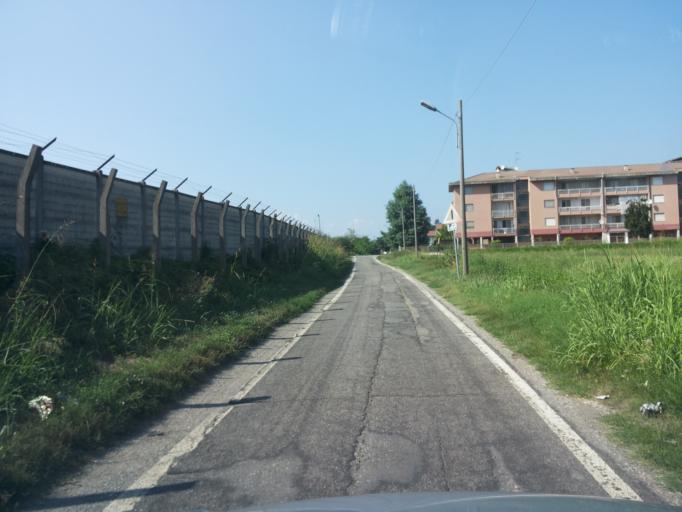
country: IT
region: Piedmont
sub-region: Provincia di Vercelli
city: Vercelli
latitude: 45.3077
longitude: 8.4332
